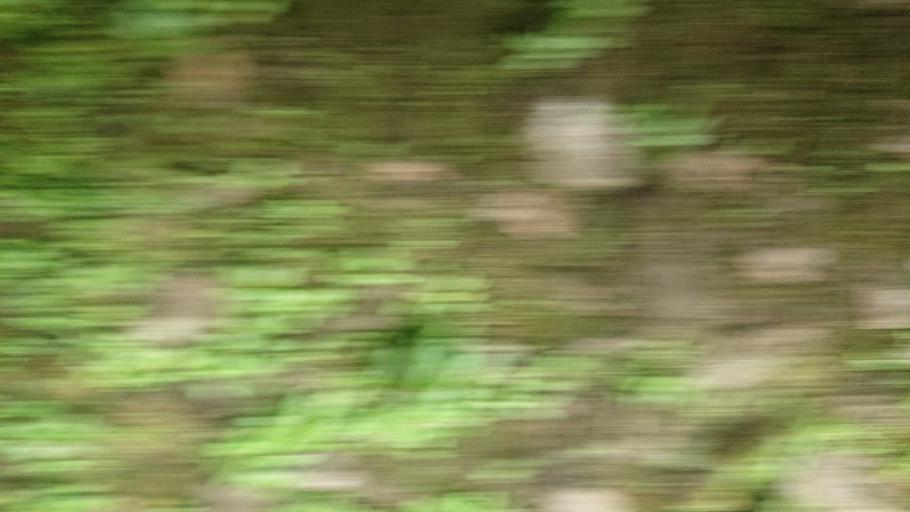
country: TW
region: Taiwan
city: Lugu
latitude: 23.8211
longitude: 120.8563
